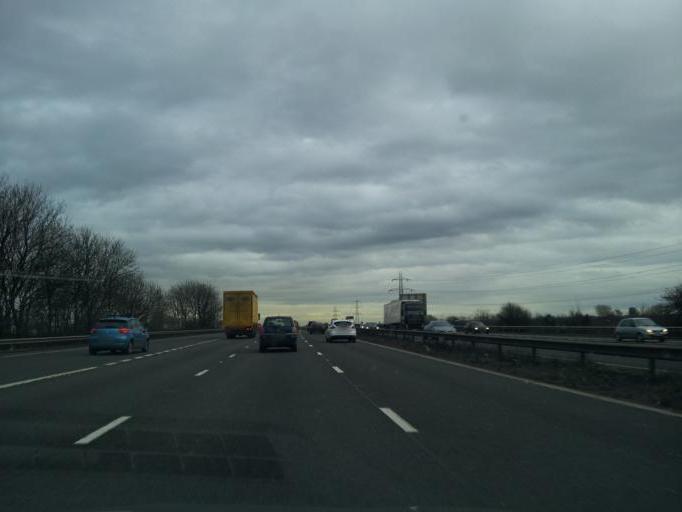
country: GB
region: England
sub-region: Warwickshire
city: Exhall
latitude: 52.4601
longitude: -1.4865
